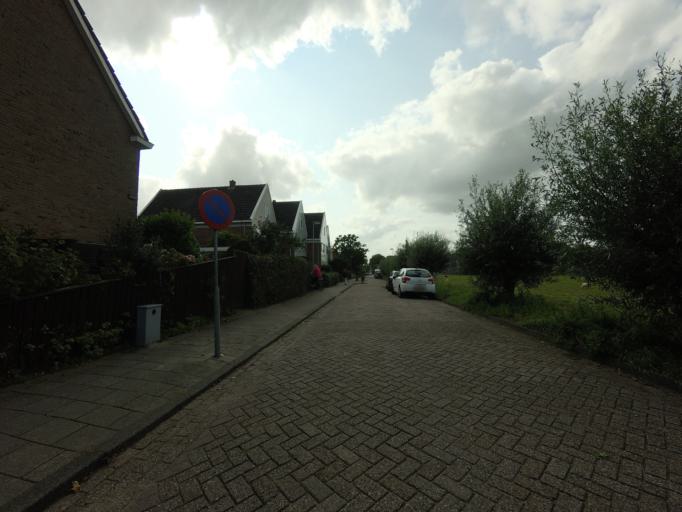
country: NL
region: North Holland
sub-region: Gemeente Waterland
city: Broek in Waterland
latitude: 52.4373
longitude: 4.9973
